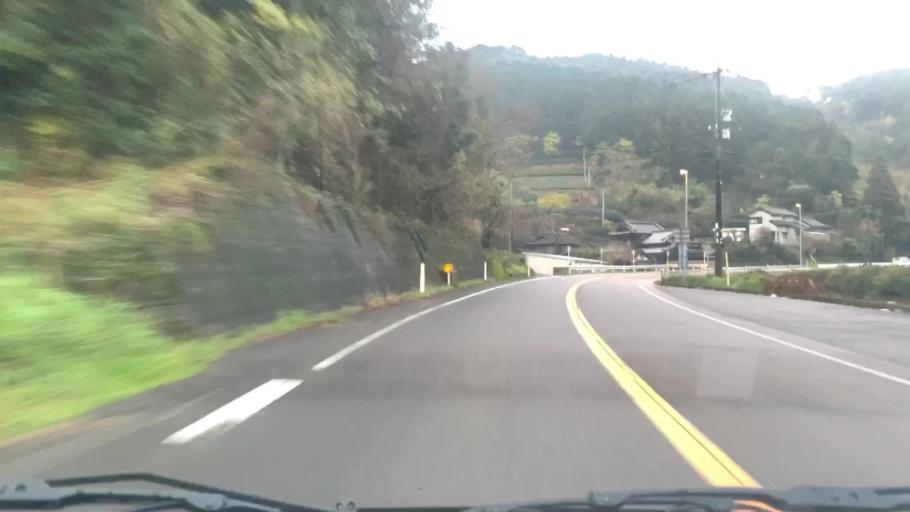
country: JP
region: Saga Prefecture
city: Ureshinomachi-shimojuku
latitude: 33.0686
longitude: 129.9635
